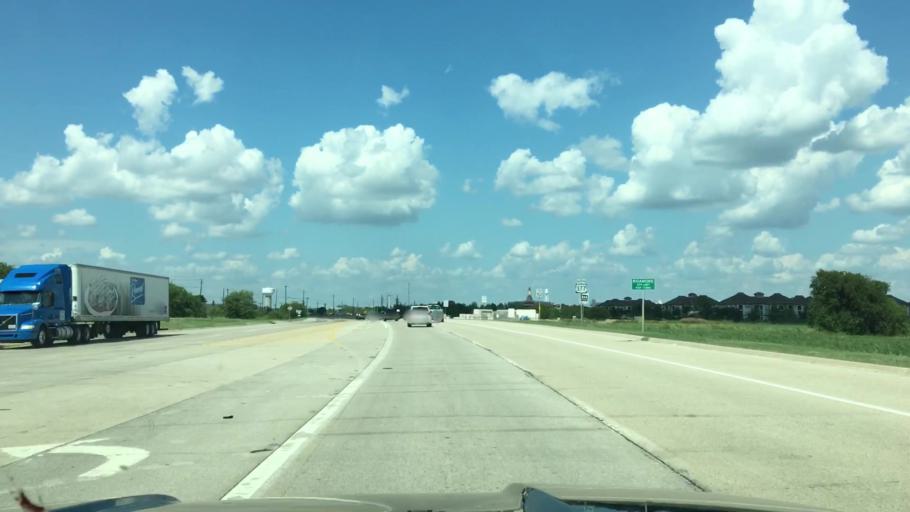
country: US
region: Texas
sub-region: Denton County
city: Roanoke
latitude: 32.9872
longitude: -97.2356
